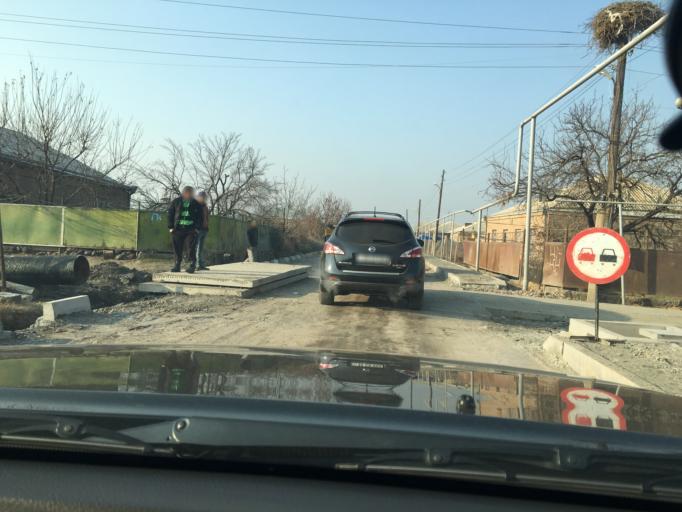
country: AM
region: Armavir
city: Janfida
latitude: 40.0414
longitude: 44.0192
